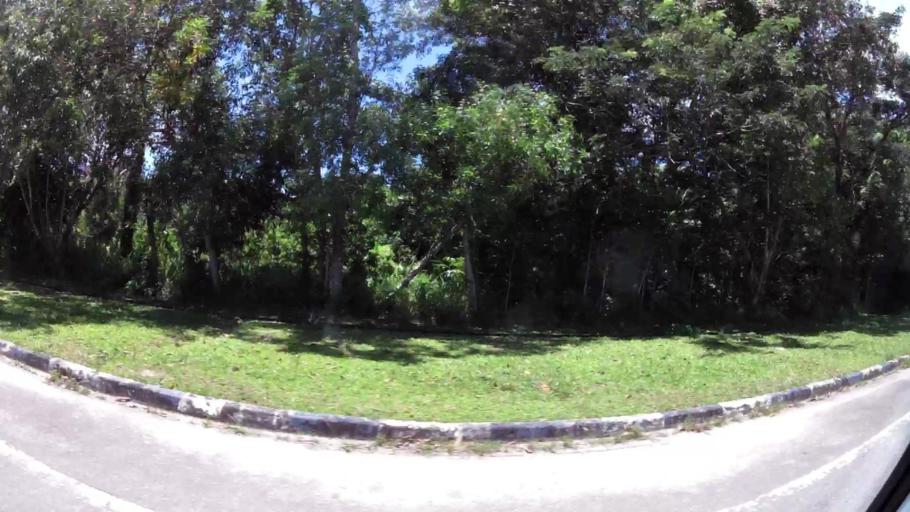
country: BN
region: Brunei and Muara
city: Bandar Seri Begawan
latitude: 4.9239
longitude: 114.9450
